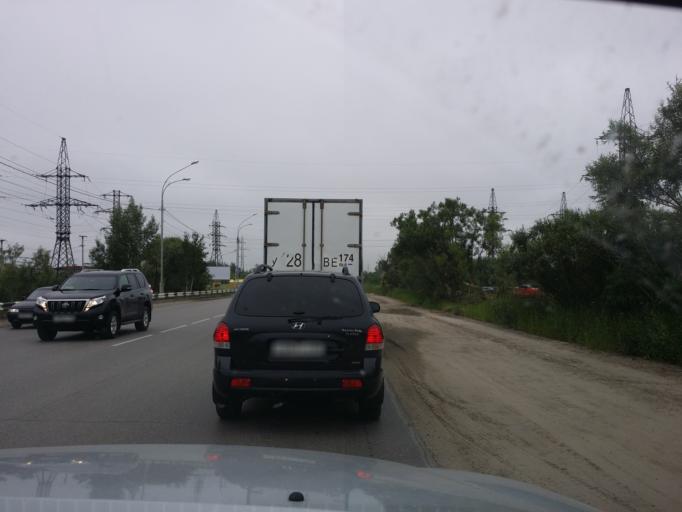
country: RU
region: Khanty-Mansiyskiy Avtonomnyy Okrug
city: Nizhnevartovsk
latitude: 60.9320
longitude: 76.5313
